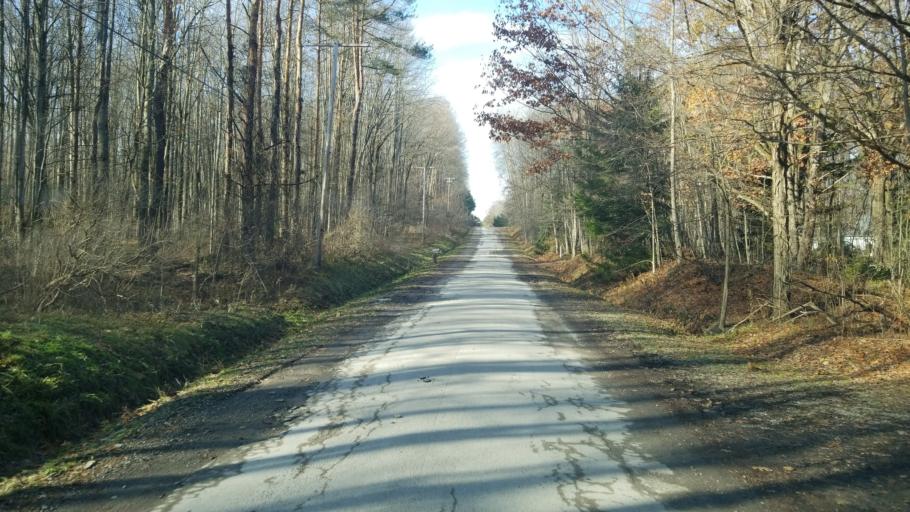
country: US
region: Ohio
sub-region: Ashtabula County
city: Roaming Shores
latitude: 41.6737
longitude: -80.8739
